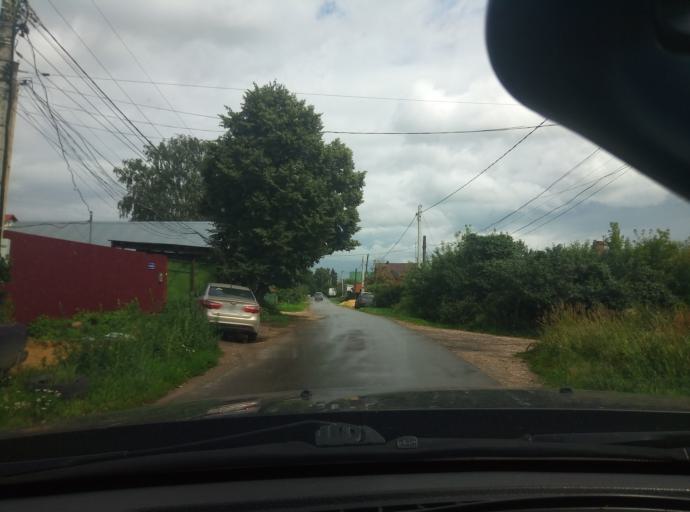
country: RU
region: Tula
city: Novomoskovsk
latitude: 53.9982
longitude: 38.3011
